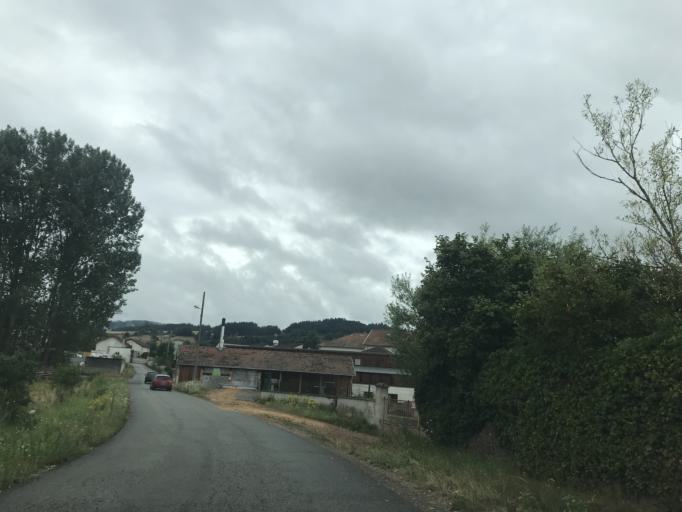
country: FR
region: Auvergne
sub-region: Departement du Puy-de-Dome
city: Arlanc
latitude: 45.4198
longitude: 3.7275
